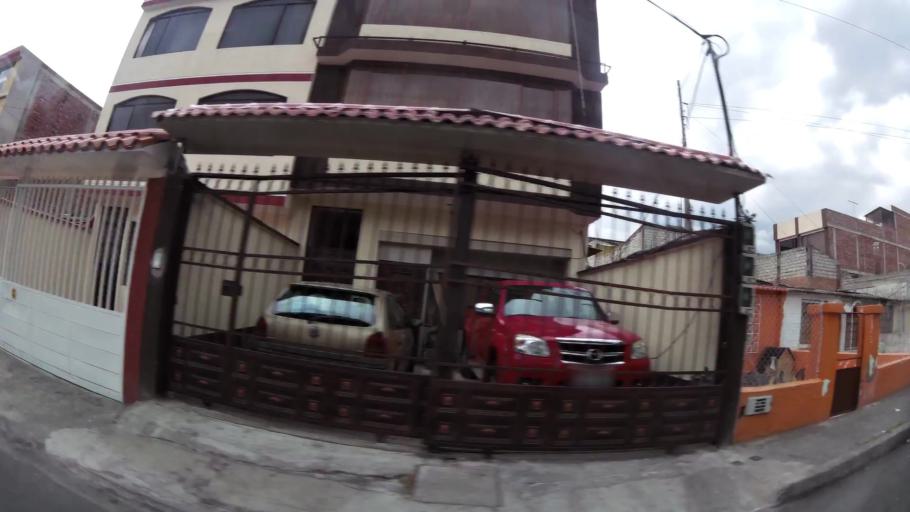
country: EC
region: Tungurahua
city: Ambato
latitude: -1.2351
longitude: -78.6140
